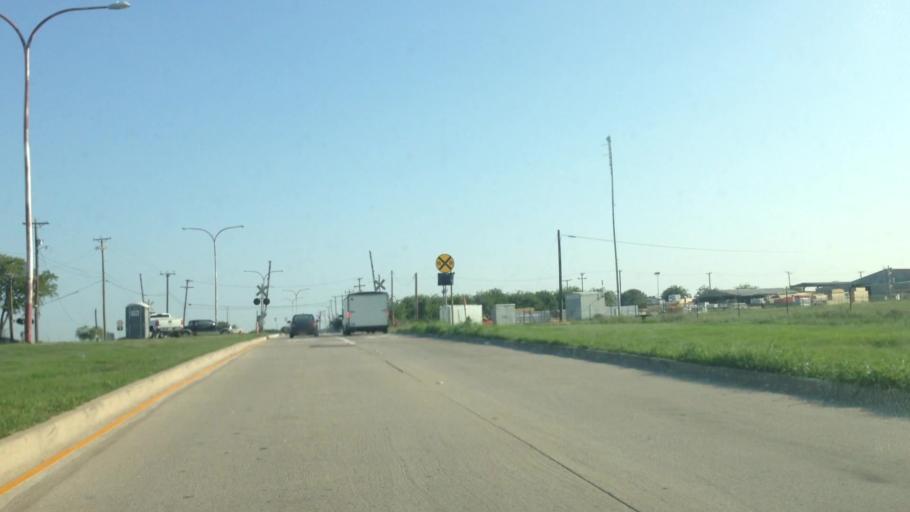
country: US
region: Texas
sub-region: Tarrant County
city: Haltom City
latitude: 32.8141
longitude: -97.3084
